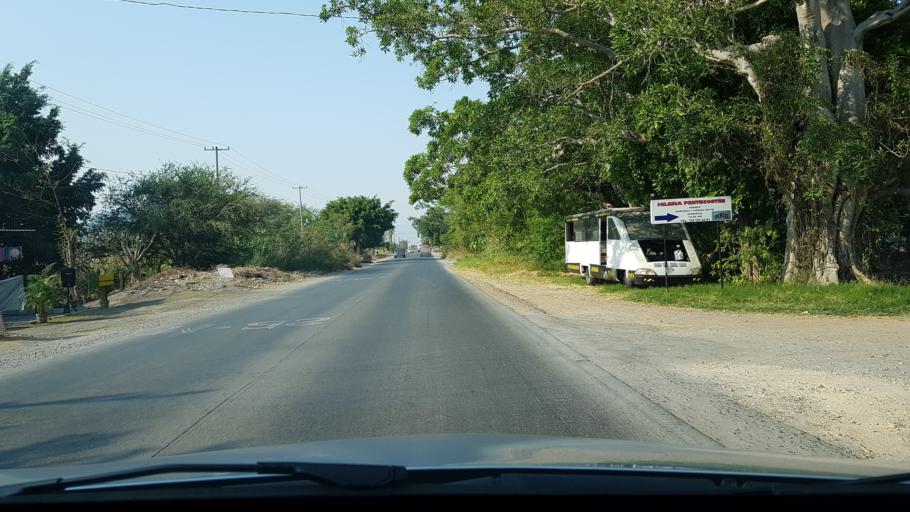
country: MX
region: Morelos
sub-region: Tlaquiltenango
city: Alfredo V. Bonfil (Chacampalco)
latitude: 18.6623
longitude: -99.1495
